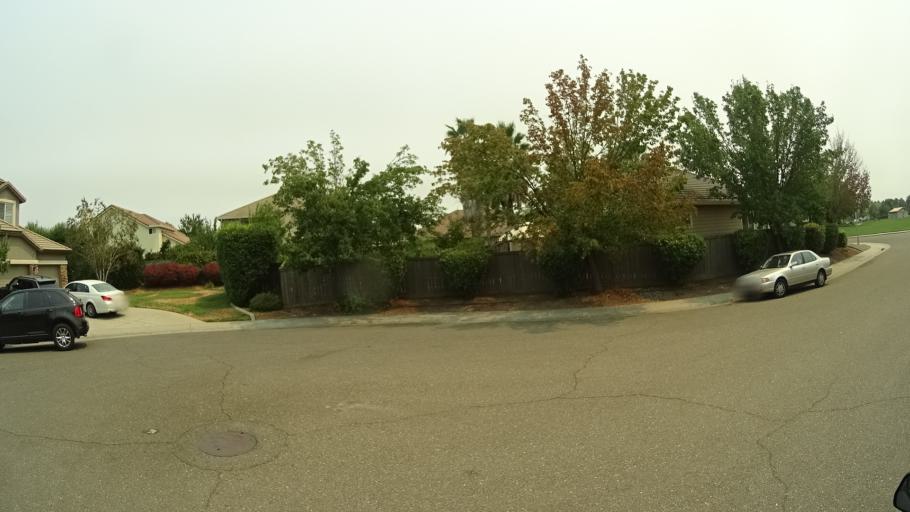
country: US
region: California
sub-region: Sacramento County
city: Laguna
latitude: 38.4068
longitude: -121.4229
